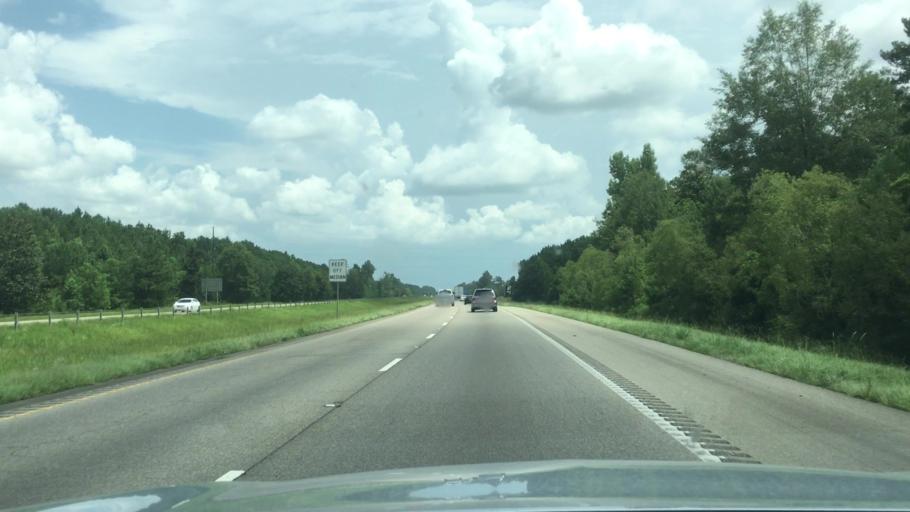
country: US
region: Mississippi
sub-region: Pearl River County
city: Nicholson
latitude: 30.4858
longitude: -89.6740
